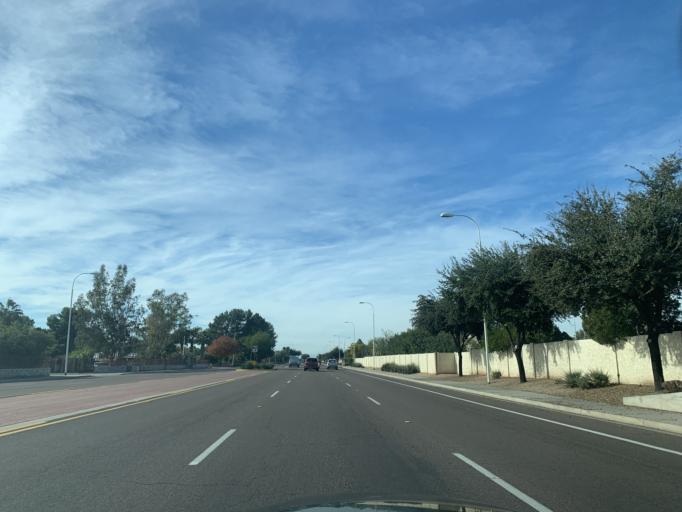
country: US
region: Arizona
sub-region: Maricopa County
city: Chandler
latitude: 33.3064
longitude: -111.8140
